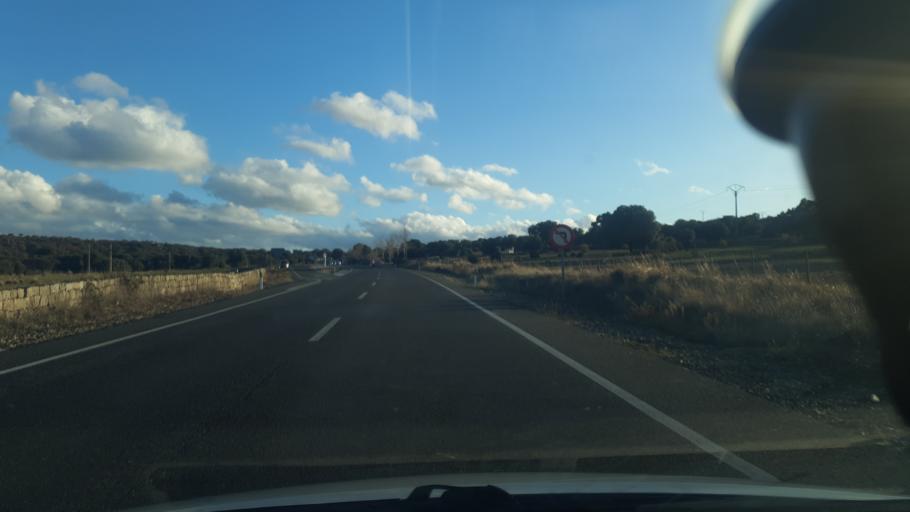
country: ES
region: Castille and Leon
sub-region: Provincia de Avila
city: Mingorria
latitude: 40.7257
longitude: -4.6748
